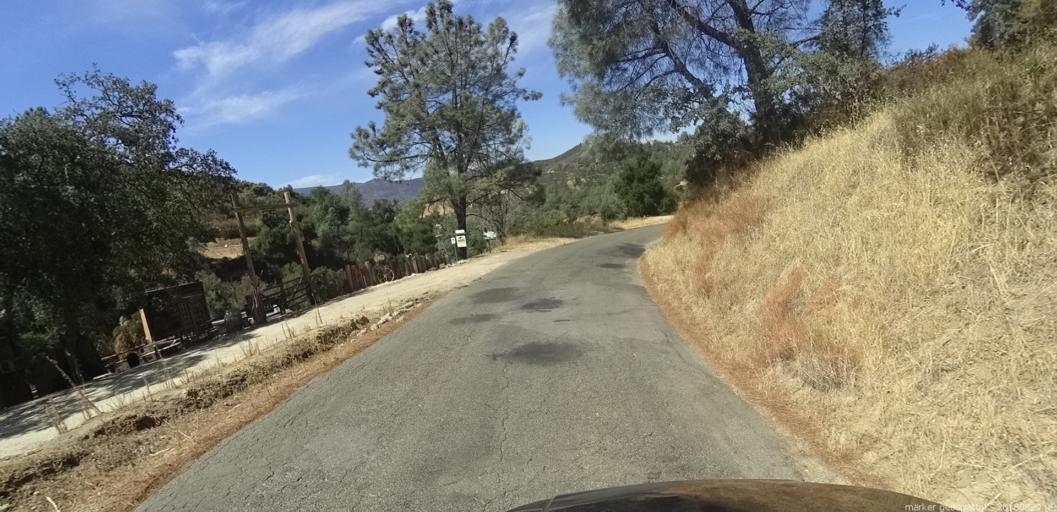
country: US
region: California
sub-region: San Luis Obispo County
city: Lake Nacimiento
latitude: 35.8218
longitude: -121.0689
